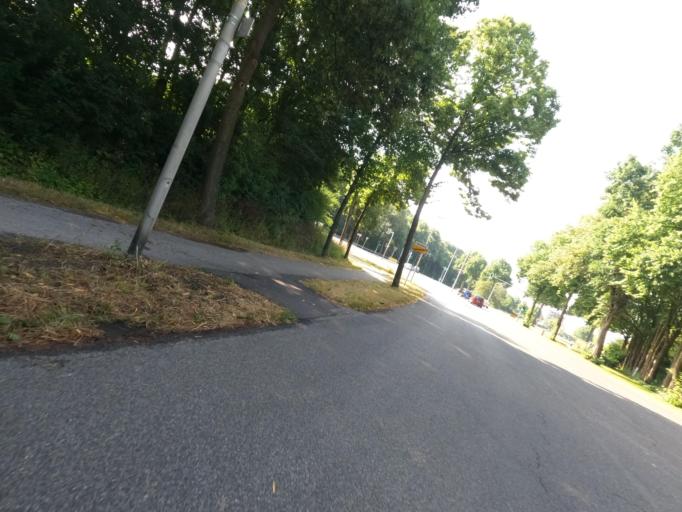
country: DE
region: North Rhine-Westphalia
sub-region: Regierungsbezirk Koln
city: Heinsberg
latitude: 51.0694
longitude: 6.0884
